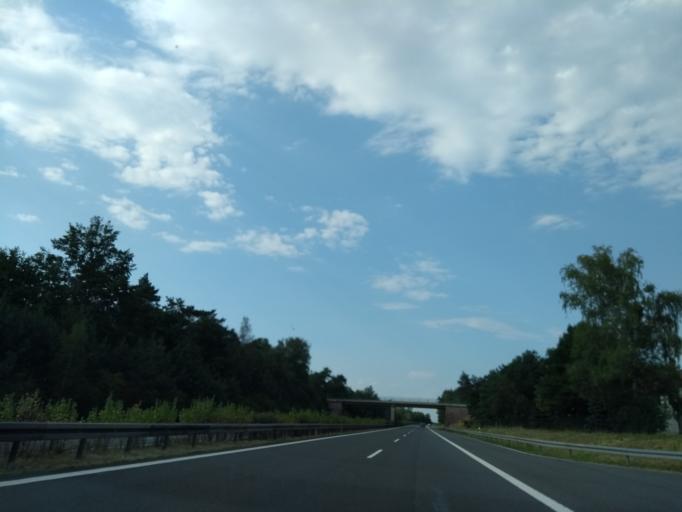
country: DE
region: Brandenburg
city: Schipkau
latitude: 51.5745
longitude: 13.9315
